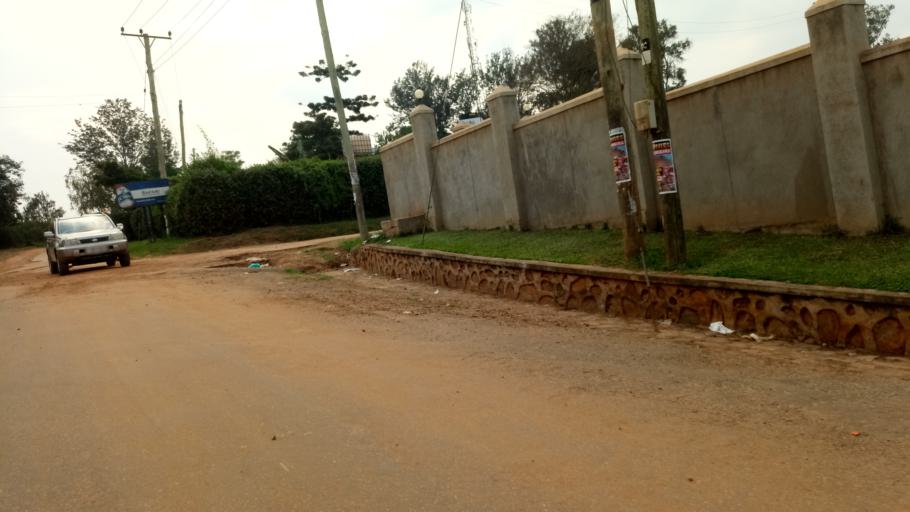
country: UG
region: Western Region
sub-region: Mbarara District
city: Mbarara
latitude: -0.6126
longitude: 30.6593
